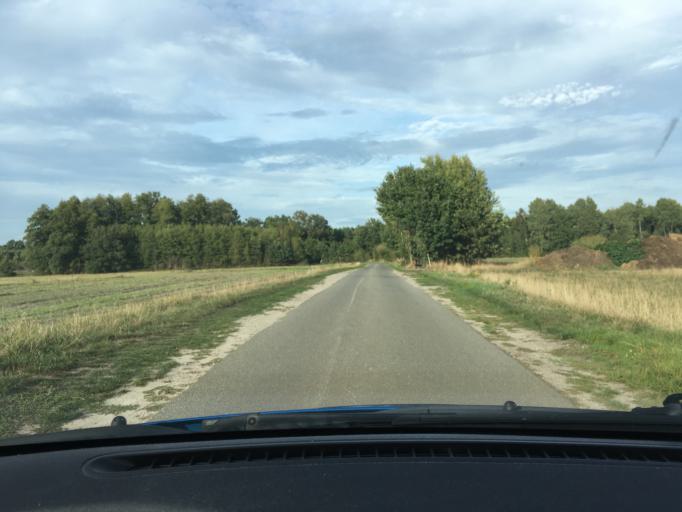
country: DE
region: Lower Saxony
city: Fassberg
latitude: 52.8889
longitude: 10.1224
